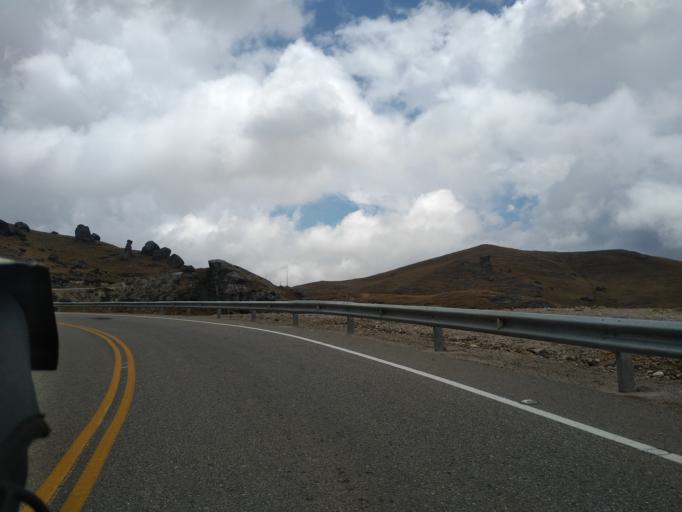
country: PE
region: La Libertad
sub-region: Provincia de Santiago de Chuco
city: Quiruvilca
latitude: -7.9733
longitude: -78.2193
